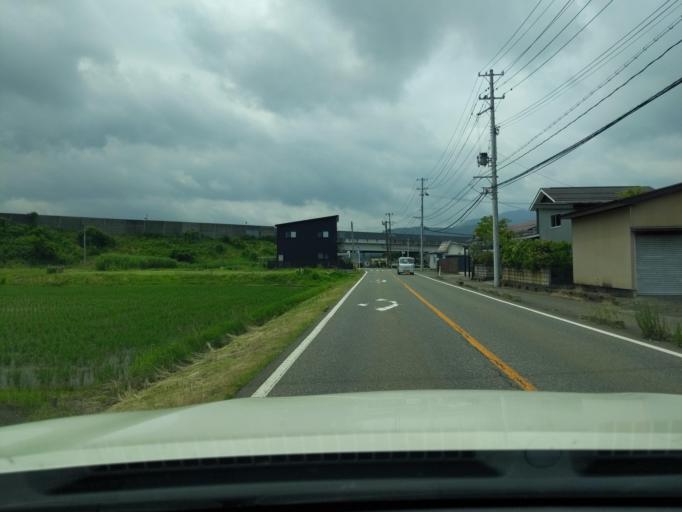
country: JP
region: Niigata
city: Kashiwazaki
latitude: 37.3449
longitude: 138.5685
